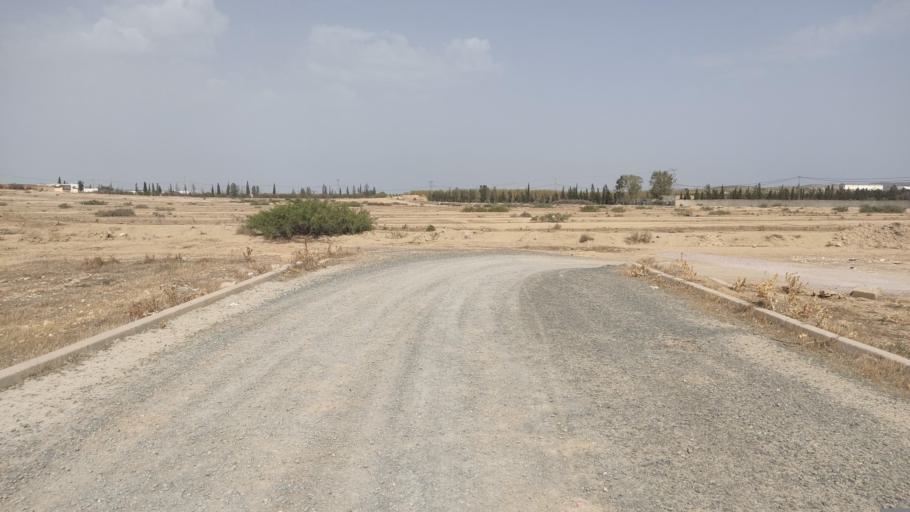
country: TN
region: Tunis
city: La Mohammedia
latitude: 36.5795
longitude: 10.1049
